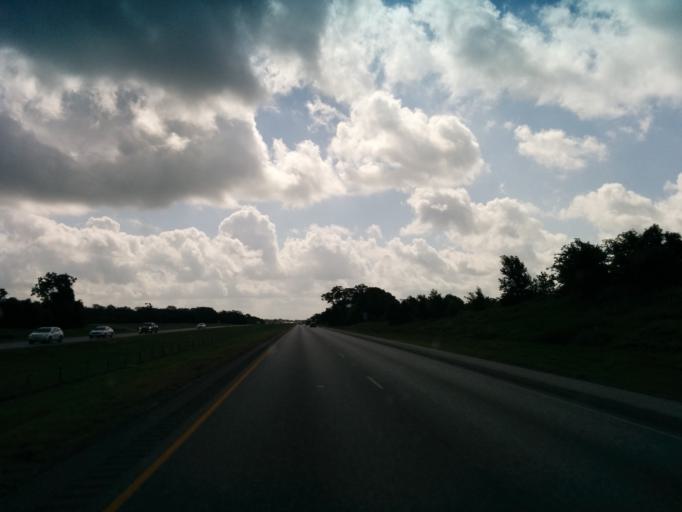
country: US
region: Texas
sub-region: Fayette County
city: Schulenburg
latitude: 29.6913
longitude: -96.9962
